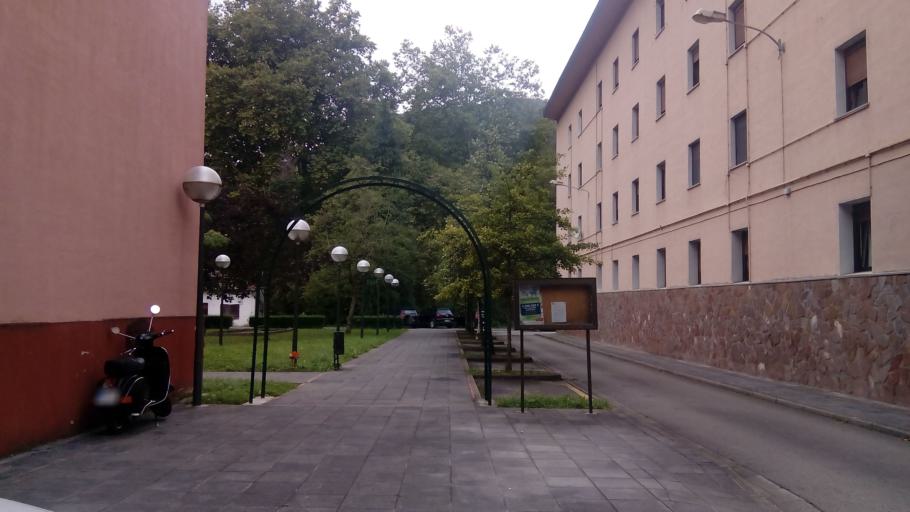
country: ES
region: Basque Country
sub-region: Provincia de Guipuzcoa
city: Andoain
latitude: 43.2237
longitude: -2.0270
